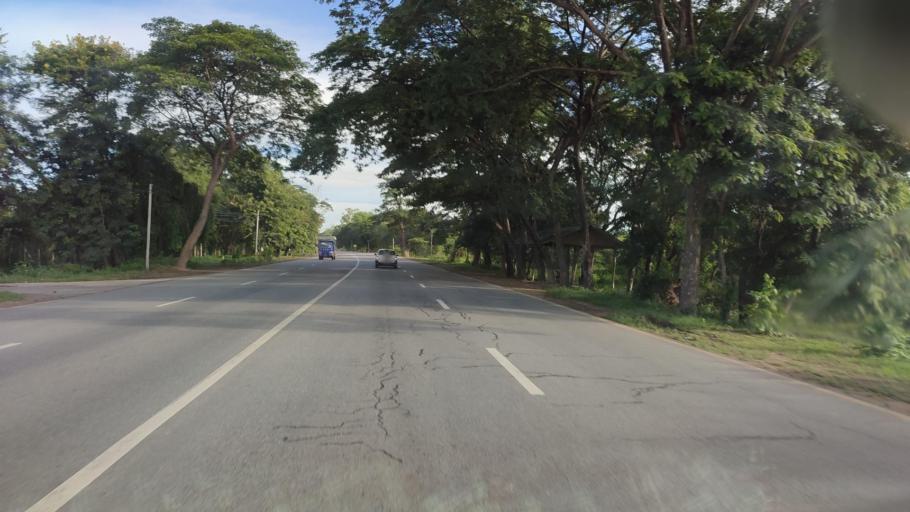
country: MM
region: Mandalay
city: Yamethin
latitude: 20.1513
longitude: 96.1924
